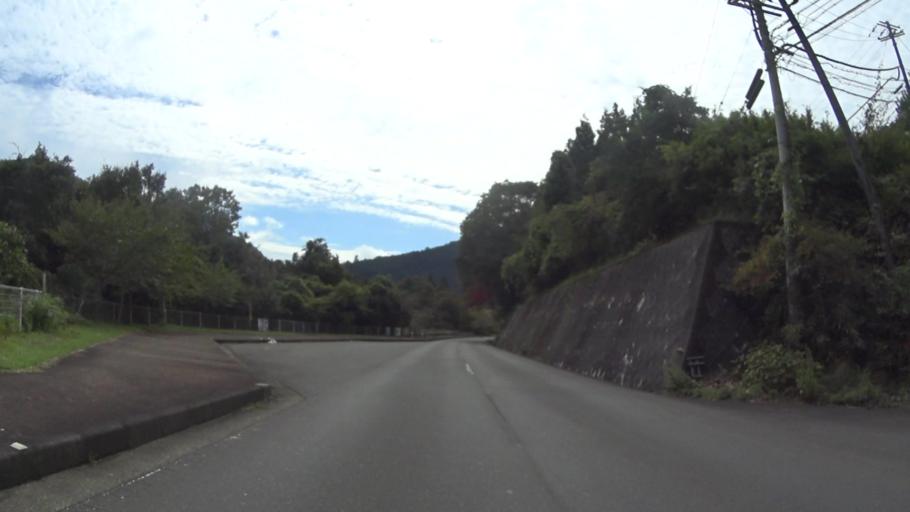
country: JP
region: Kyoto
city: Maizuru
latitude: 35.2674
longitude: 135.4940
